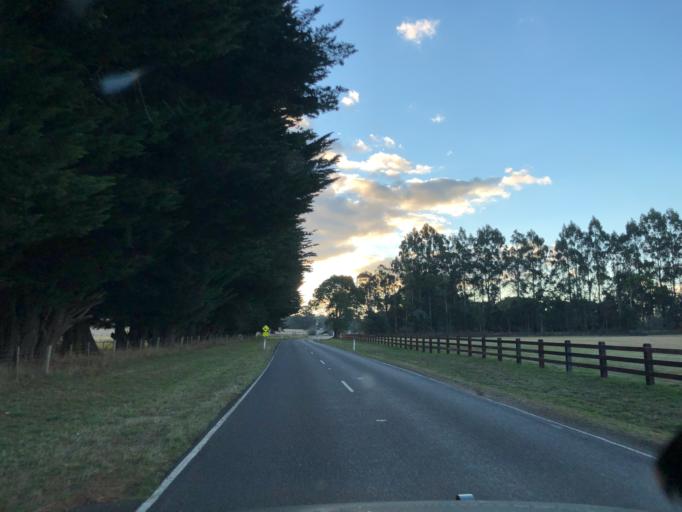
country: AU
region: Victoria
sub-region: Moorabool
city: Bacchus Marsh
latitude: -37.4187
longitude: 144.2870
